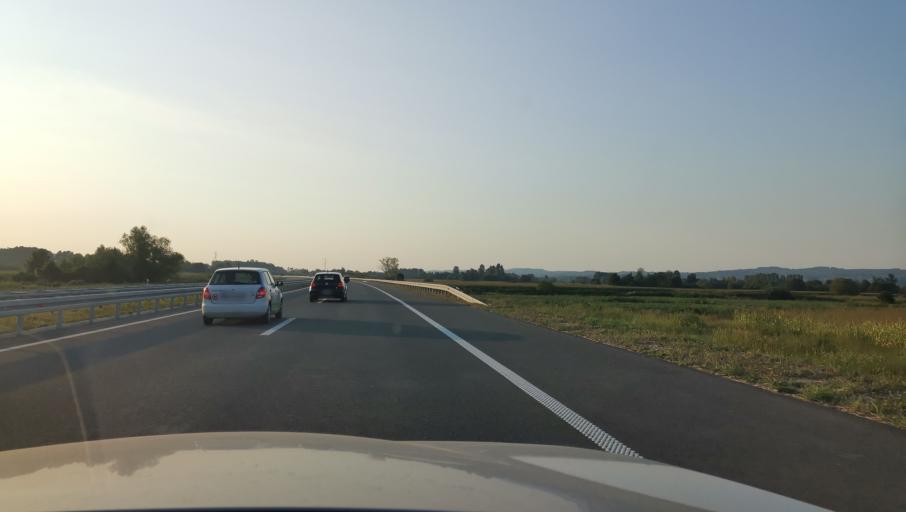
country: RS
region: Central Serbia
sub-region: Kolubarski Okrug
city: Ljig
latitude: 44.2775
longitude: 20.2635
